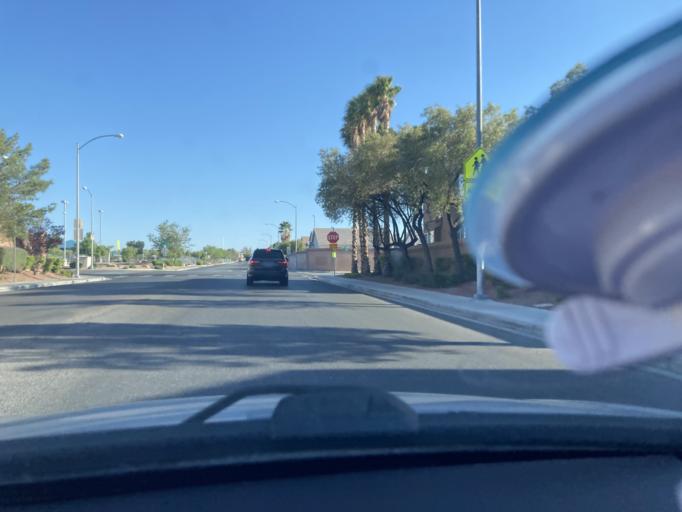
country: US
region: Nevada
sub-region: Clark County
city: Enterprise
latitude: 36.0634
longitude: -115.2930
